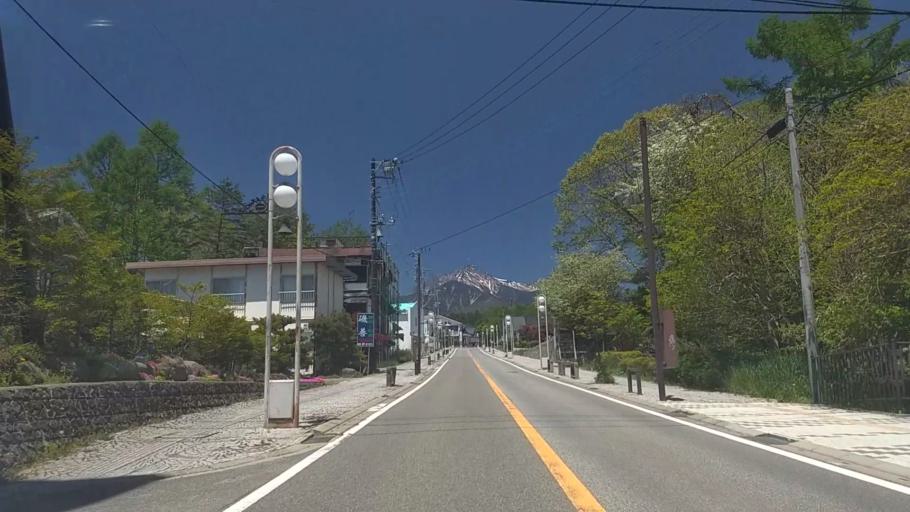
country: JP
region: Yamanashi
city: Nirasaki
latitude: 35.9164
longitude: 138.4402
